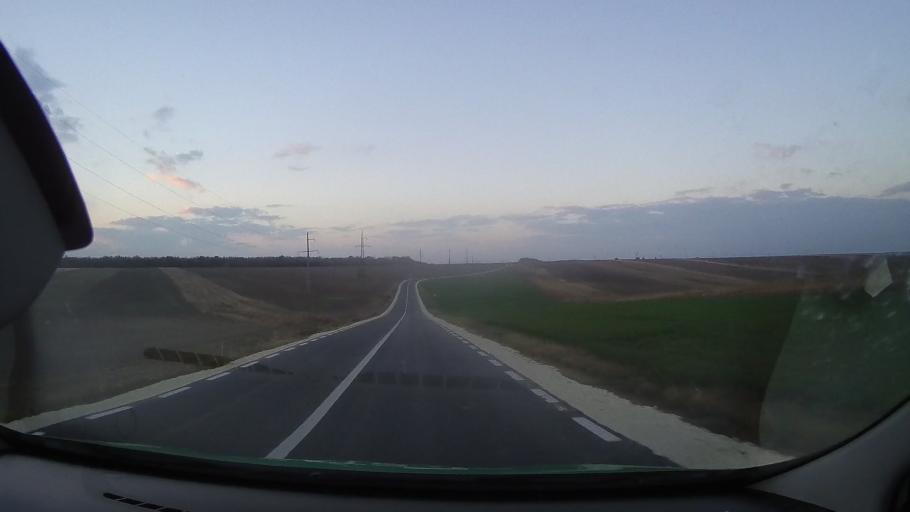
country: RO
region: Constanta
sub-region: Comuna Baneasa
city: Baneasa
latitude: 44.1038
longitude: 27.6738
